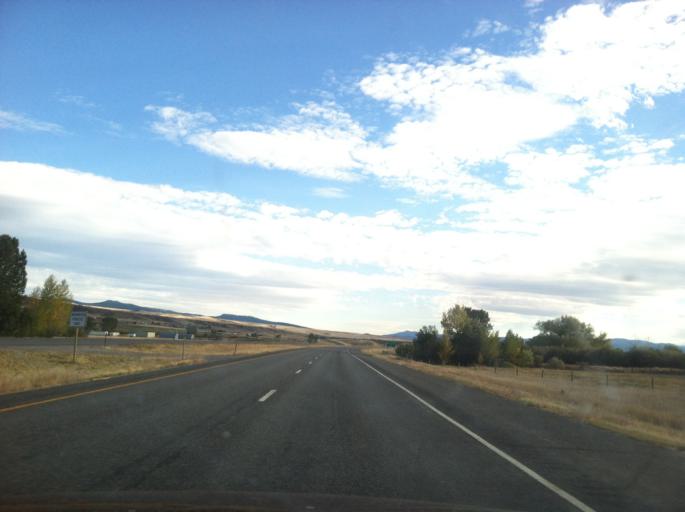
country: US
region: Montana
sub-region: Deer Lodge County
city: Warm Springs
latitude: 46.2770
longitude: -112.7474
